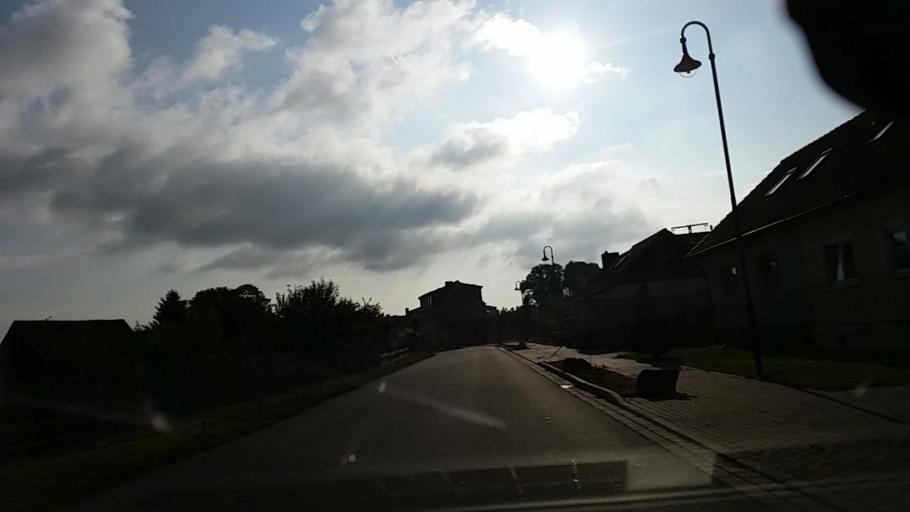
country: DE
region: Thuringia
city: Nohra
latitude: 51.4332
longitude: 10.7003
